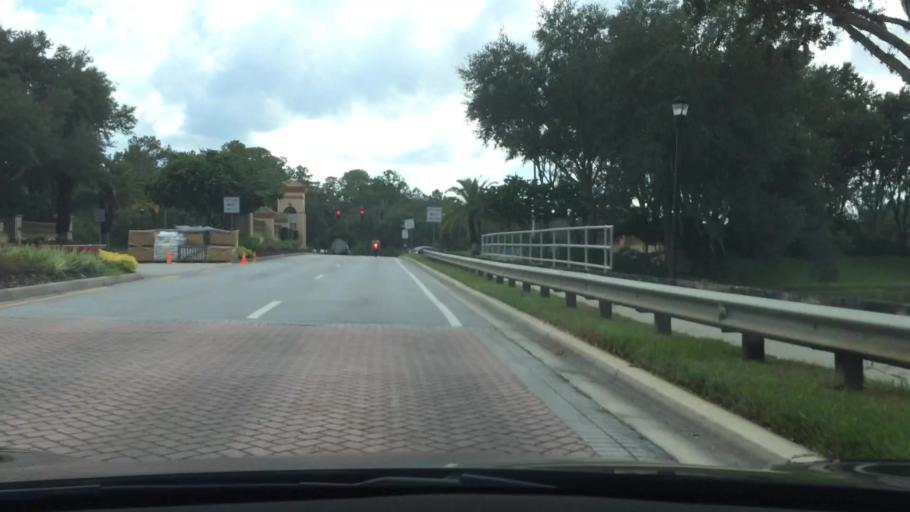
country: US
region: Florida
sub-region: Hillsborough County
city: Pebble Creek
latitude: 28.1722
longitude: -82.3646
